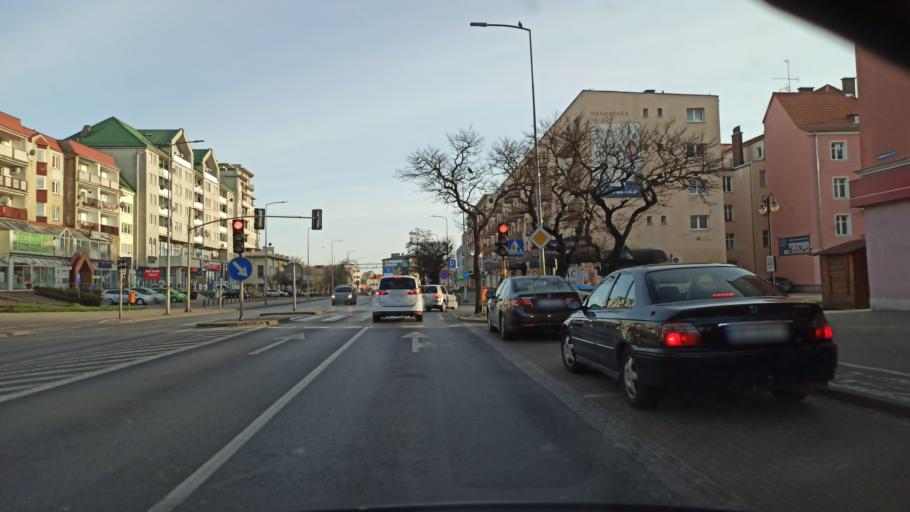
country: PL
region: Warmian-Masurian Voivodeship
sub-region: Powiat elblaski
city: Elblag
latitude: 54.1585
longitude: 19.4044
